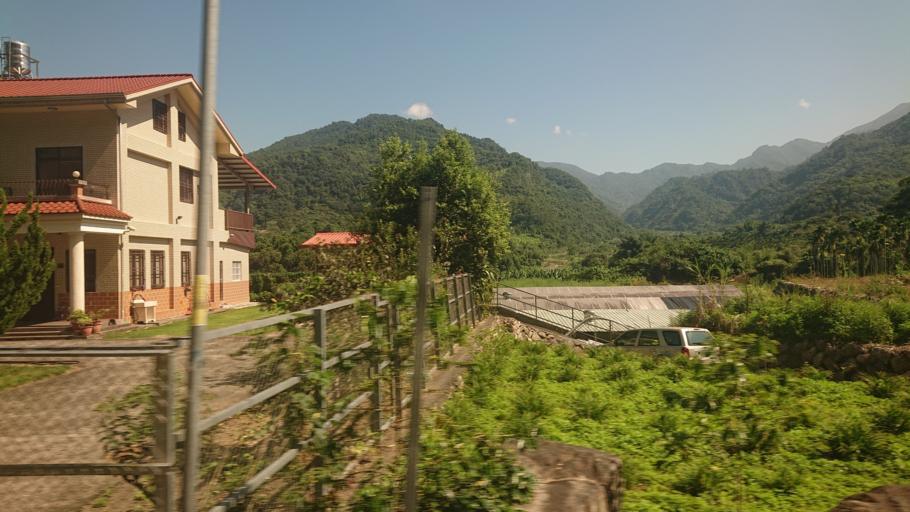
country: TW
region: Taiwan
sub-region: Nantou
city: Puli
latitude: 24.0625
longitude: 120.9473
